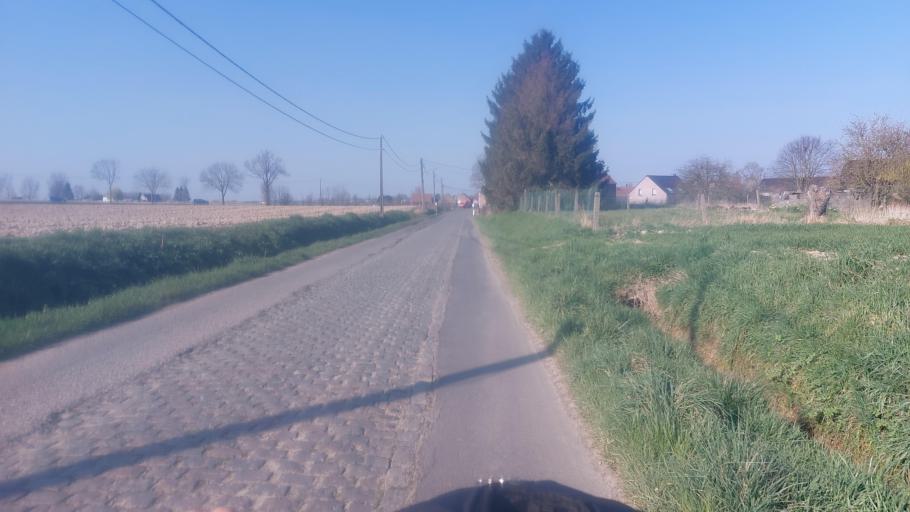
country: BE
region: Wallonia
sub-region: Province du Hainaut
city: Brugelette
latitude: 50.6432
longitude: 3.8411
